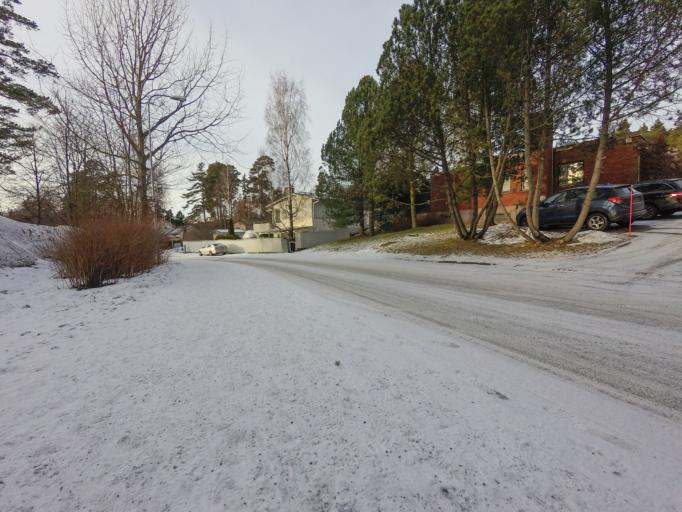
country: FI
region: Uusimaa
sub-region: Helsinki
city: Helsinki
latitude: 60.1626
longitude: 25.0516
